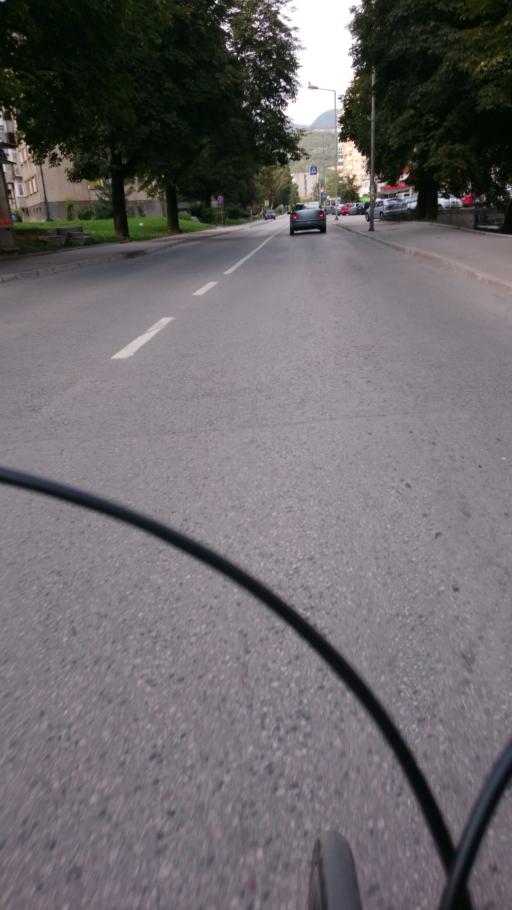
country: BA
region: Federation of Bosnia and Herzegovina
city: Zenica
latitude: 44.2019
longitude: 17.9206
